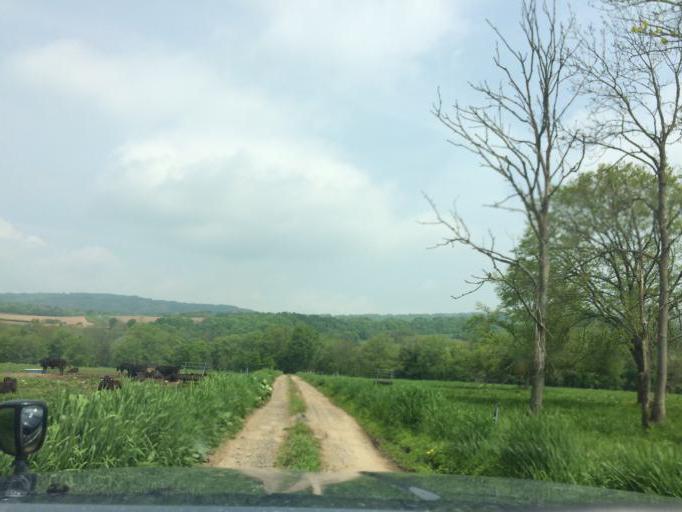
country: JP
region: Hokkaido
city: Niseko Town
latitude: 42.6729
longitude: 140.6006
